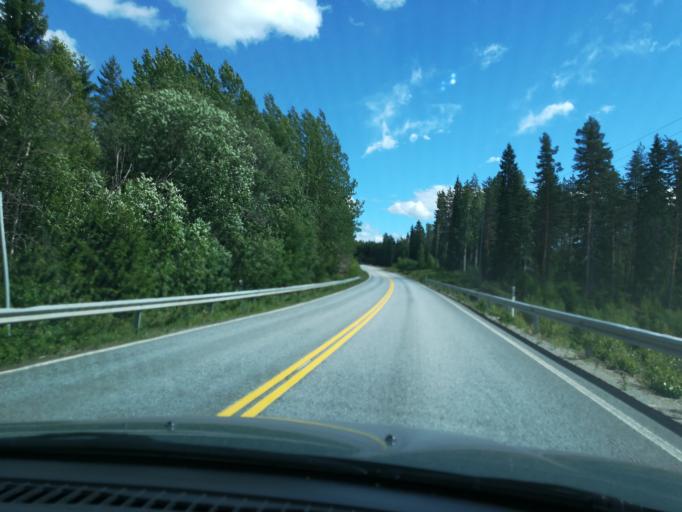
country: FI
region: Southern Savonia
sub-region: Mikkeli
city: Hirvensalmi
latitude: 61.6559
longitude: 26.9927
